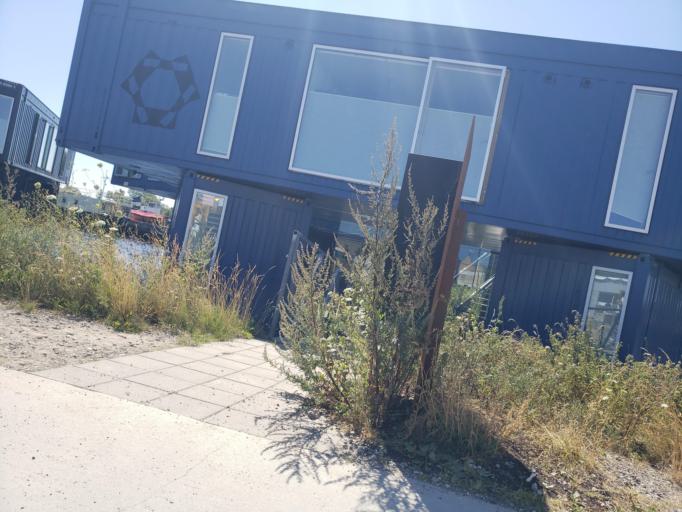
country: DK
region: Capital Region
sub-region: Kobenhavn
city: Christianshavn
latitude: 55.6906
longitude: 12.6087
